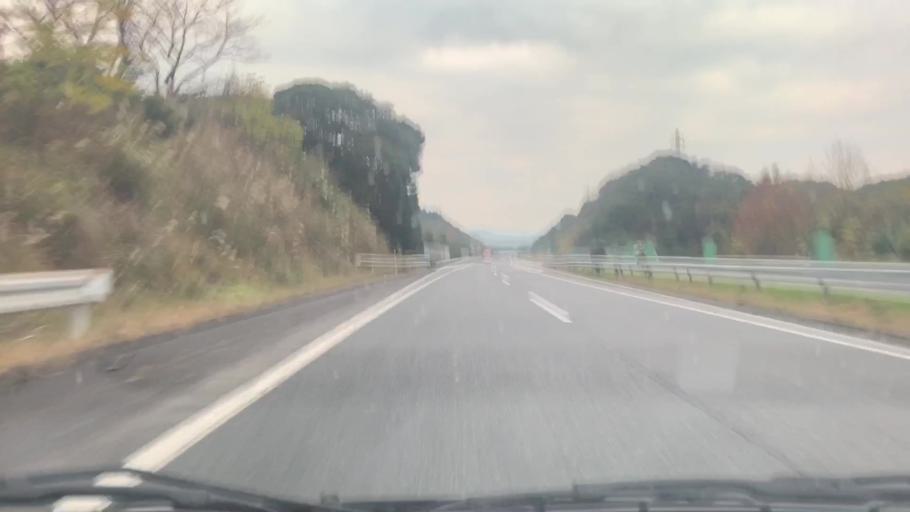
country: JP
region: Nagasaki
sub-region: Isahaya-shi
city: Isahaya
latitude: 32.8221
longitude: 129.9979
